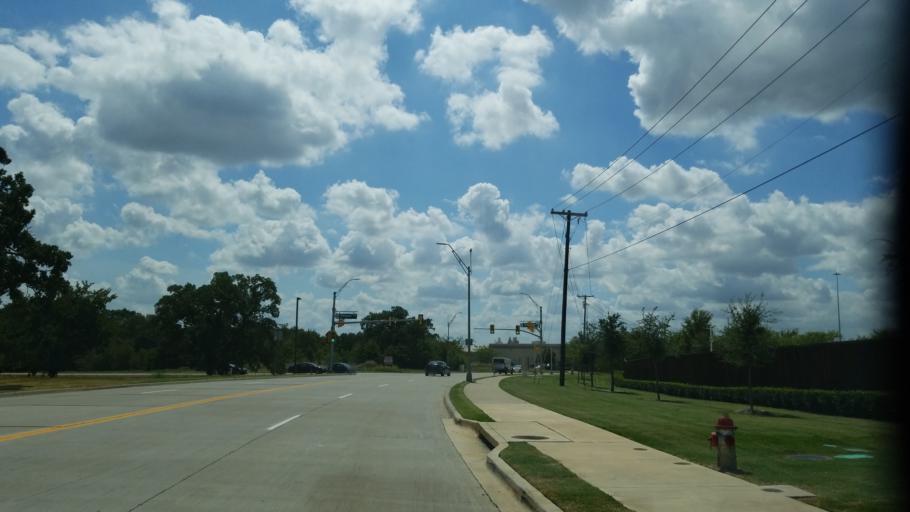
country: US
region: Texas
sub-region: Tarrant County
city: Grapevine
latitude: 32.9062
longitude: -97.0944
